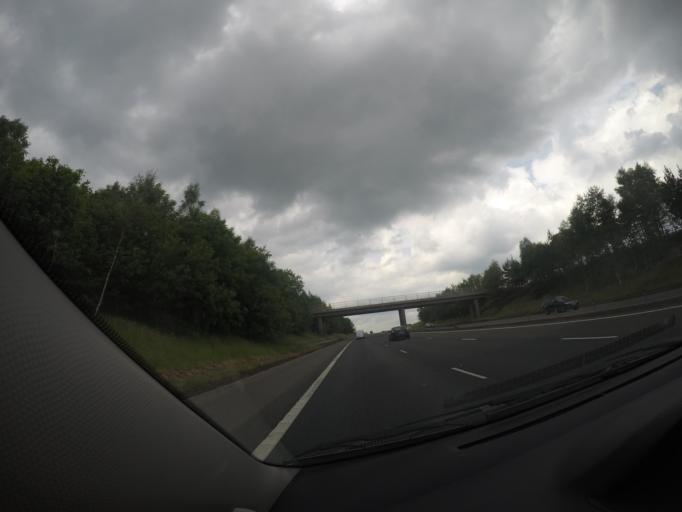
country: GB
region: Scotland
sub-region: Dumfries and Galloway
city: Moffat
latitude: 55.2624
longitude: -3.4167
